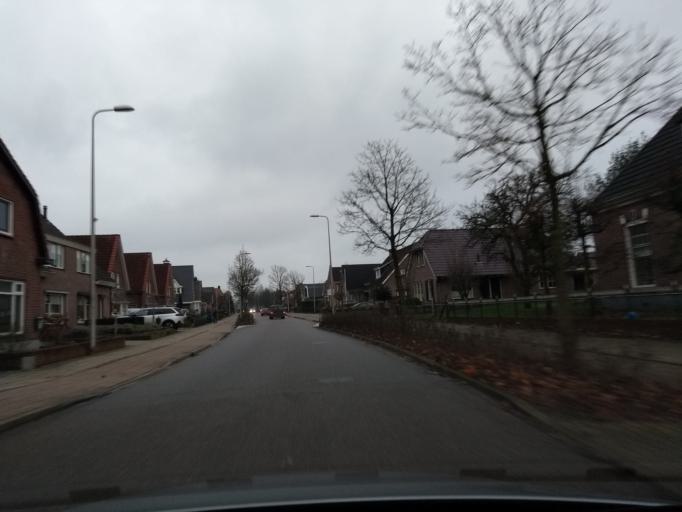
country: NL
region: Overijssel
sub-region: Gemeente Hof van Twente
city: Markelo
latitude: 52.2792
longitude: 6.4268
